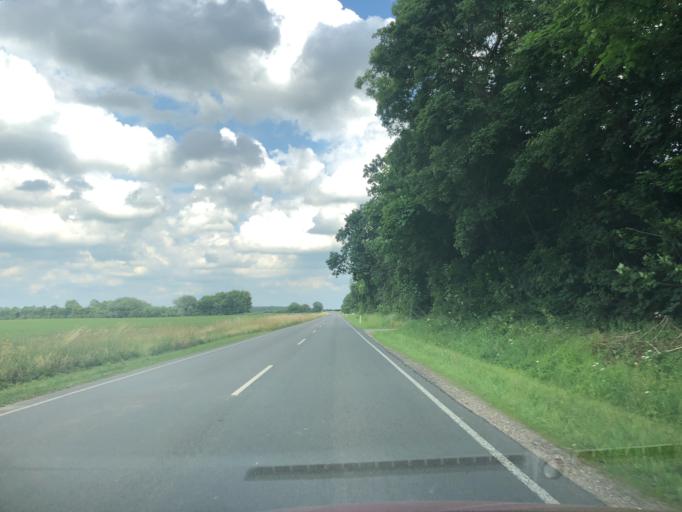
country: DK
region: Zealand
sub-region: Faxe Kommune
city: Fakse
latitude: 55.3140
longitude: 12.1445
